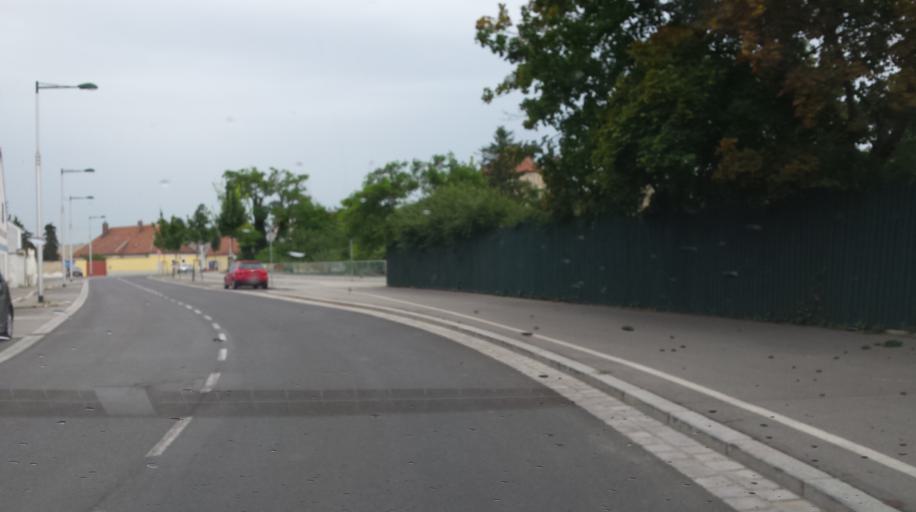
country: AT
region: Burgenland
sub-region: Politischer Bezirk Neusiedl am See
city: Bruckneudorf
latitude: 48.0201
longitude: 16.7756
